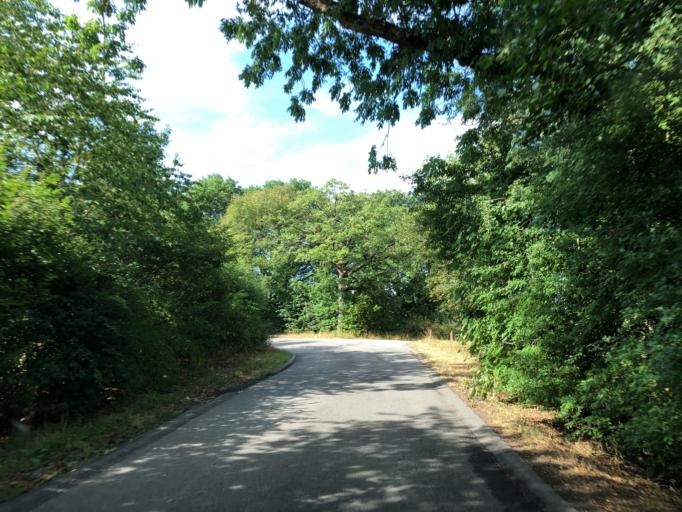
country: DK
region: South Denmark
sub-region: Vejle Kommune
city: Egtved
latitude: 55.6544
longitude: 9.3025
